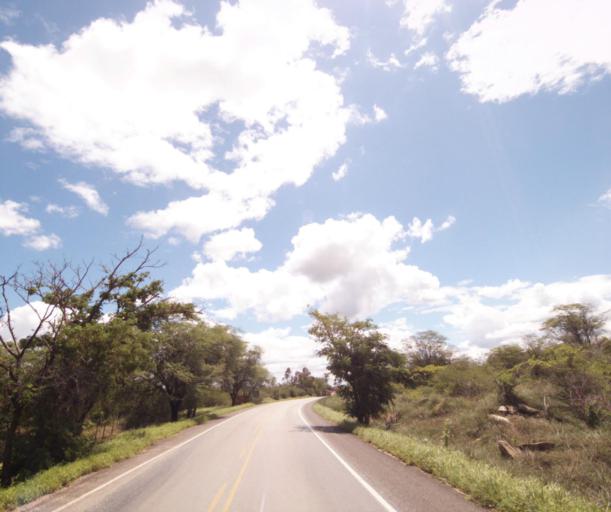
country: BR
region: Bahia
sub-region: Brumado
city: Brumado
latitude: -14.2448
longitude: -41.7279
